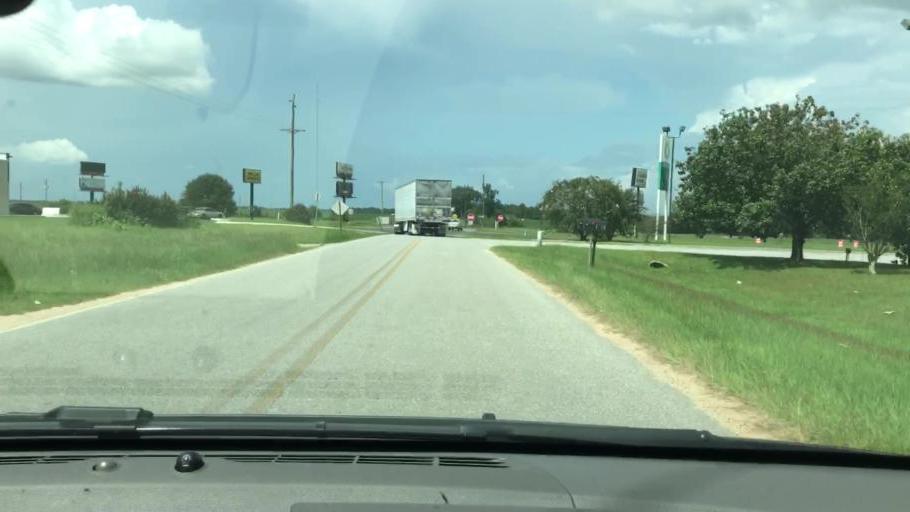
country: US
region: Georgia
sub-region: Seminole County
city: Donalsonville
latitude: 31.0906
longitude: -84.9963
